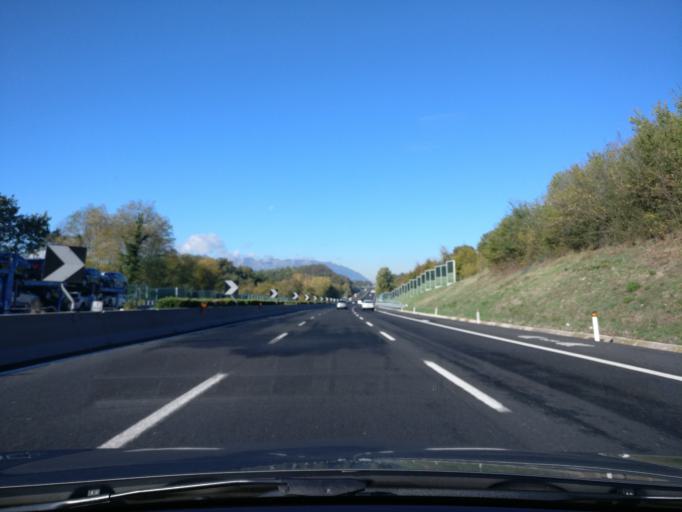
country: IT
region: Latium
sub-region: Provincia di Frosinone
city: Pofi
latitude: 41.5589
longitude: 13.4109
